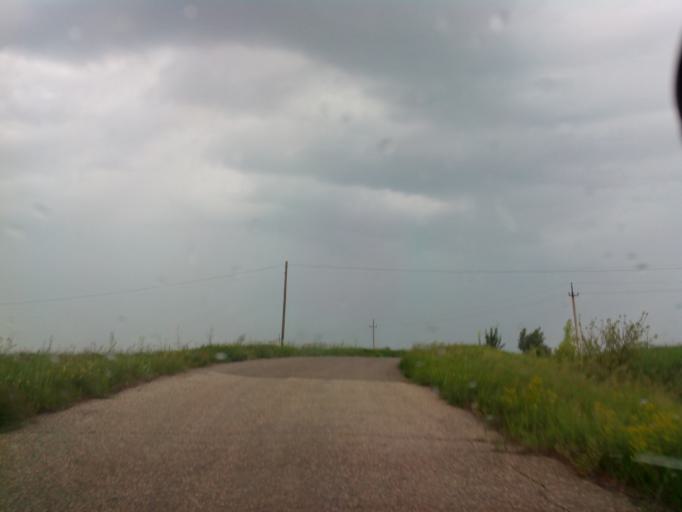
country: RU
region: Volgograd
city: Slashchevskaya
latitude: 49.7770
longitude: 42.4541
